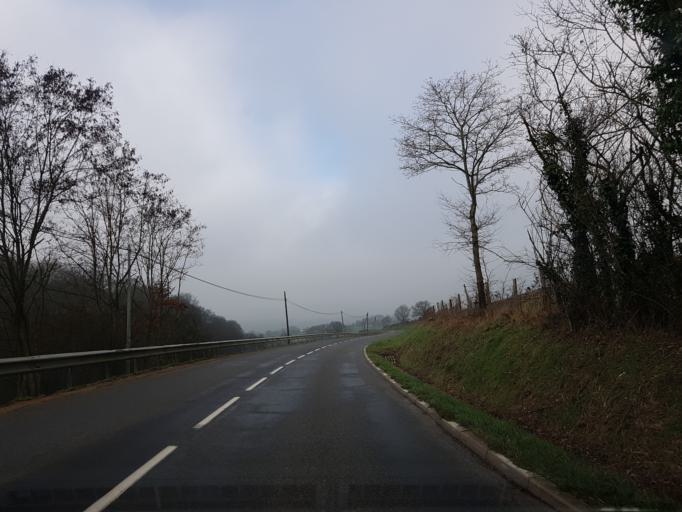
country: FR
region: Bourgogne
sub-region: Departement de Saone-et-Loire
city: Toulon-sur-Arroux
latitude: 46.6858
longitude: 4.1653
